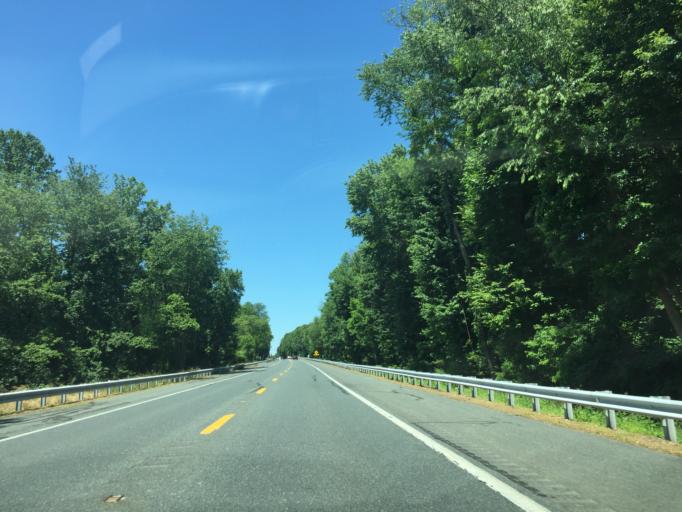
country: US
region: Maryland
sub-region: Harford County
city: Bel Air North
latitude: 39.5760
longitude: -76.3961
